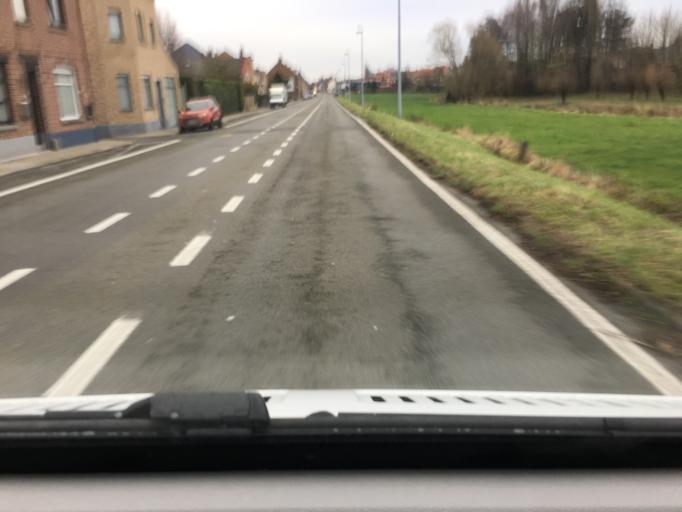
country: BE
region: Flanders
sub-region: Provincie West-Vlaanderen
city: Wervik
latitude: 50.7783
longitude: 3.0251
